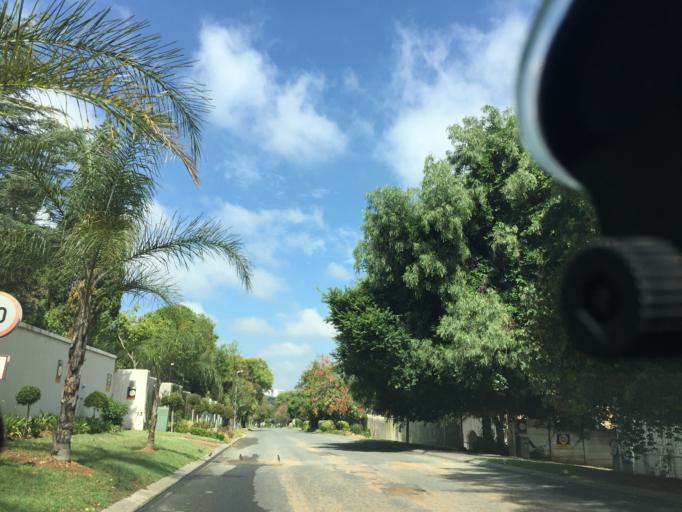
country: ZA
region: Gauteng
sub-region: City of Johannesburg Metropolitan Municipality
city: Modderfontein
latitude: -26.0805
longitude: 28.0789
